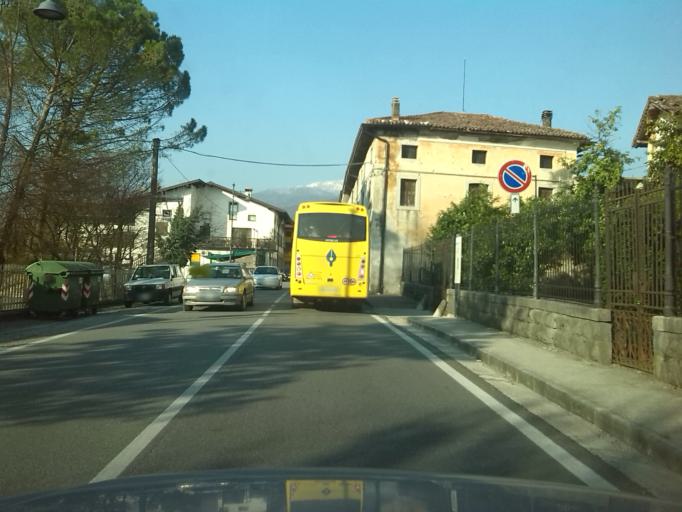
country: IT
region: Friuli Venezia Giulia
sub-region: Provincia di Udine
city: San Pietro al Natisone
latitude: 46.1279
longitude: 13.4856
